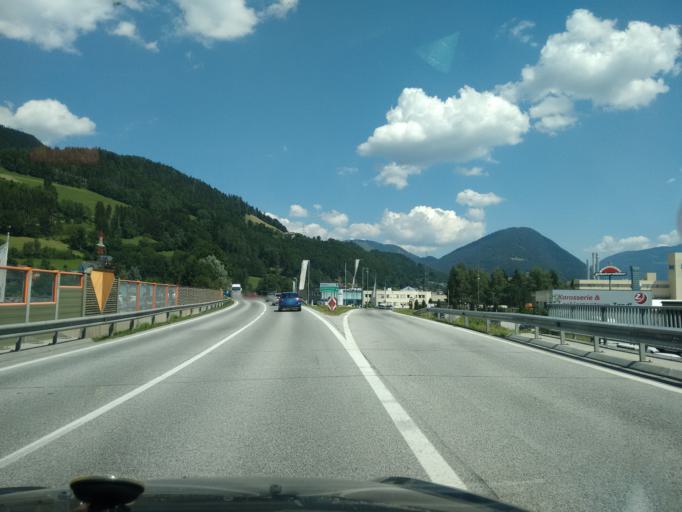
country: AT
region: Styria
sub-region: Politischer Bezirk Liezen
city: Weissenbach bei Liezen
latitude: 47.5671
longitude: 14.2062
